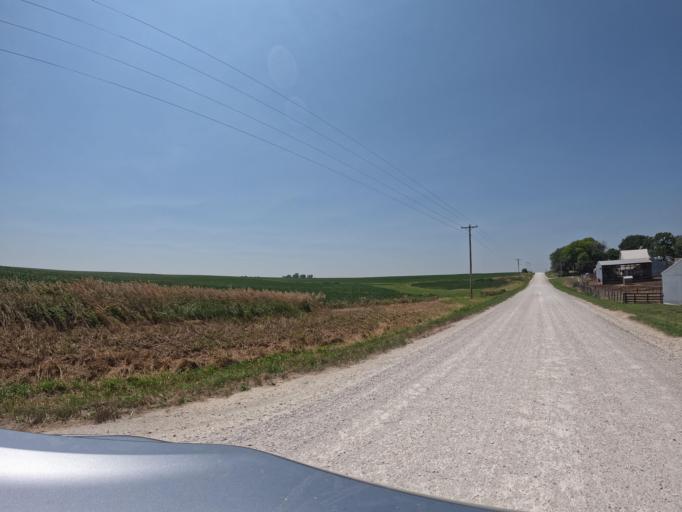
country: US
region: Iowa
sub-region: Keokuk County
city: Sigourney
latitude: 41.2866
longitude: -92.2124
